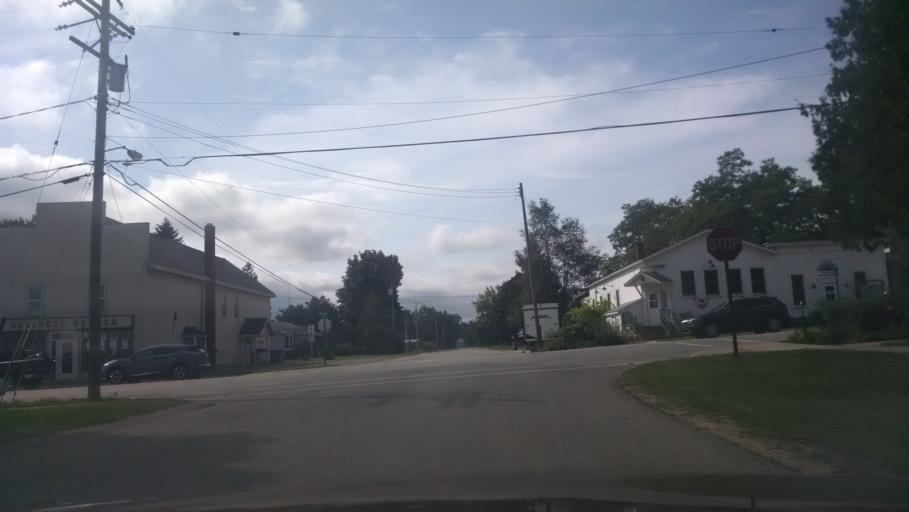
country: US
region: Michigan
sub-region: Leelanau County
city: Leland
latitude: 44.9747
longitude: -85.6525
